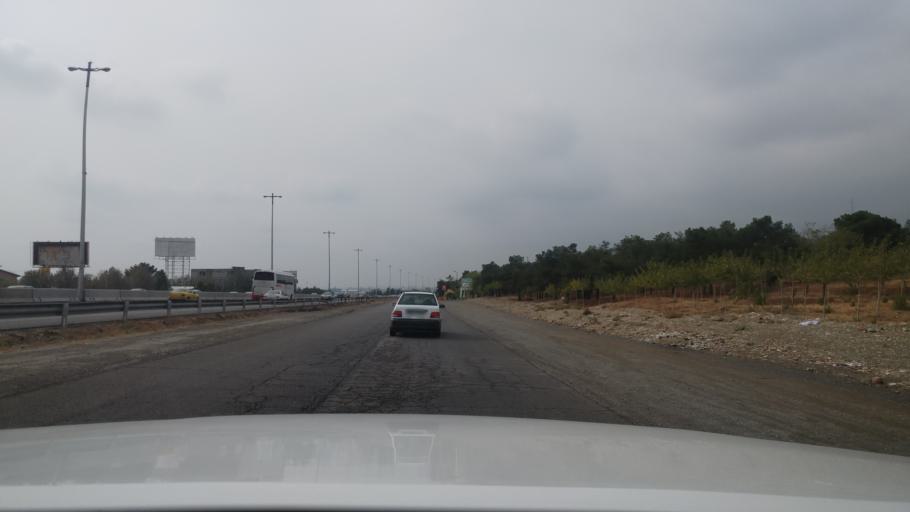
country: IR
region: Tehran
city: Shahr-e Qods
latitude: 35.7185
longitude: 51.2208
